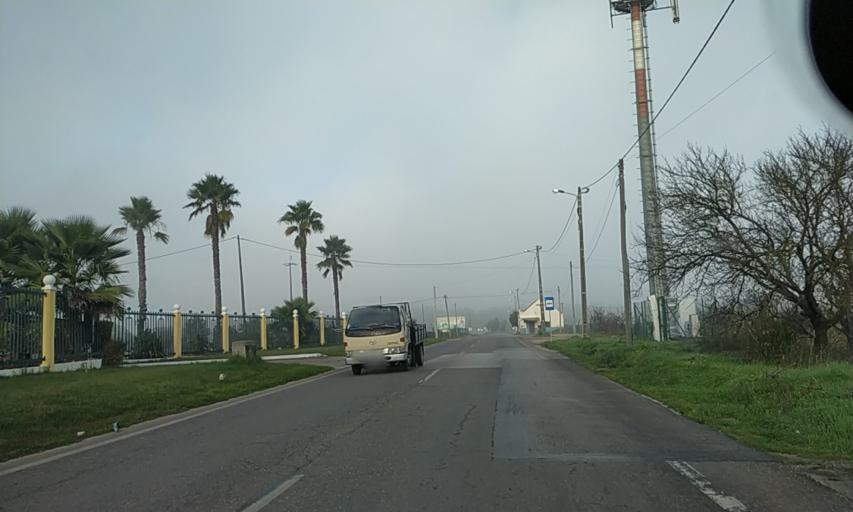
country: PT
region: Setubal
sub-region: Palmela
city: Pinhal Novo
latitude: 38.6028
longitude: -8.9032
